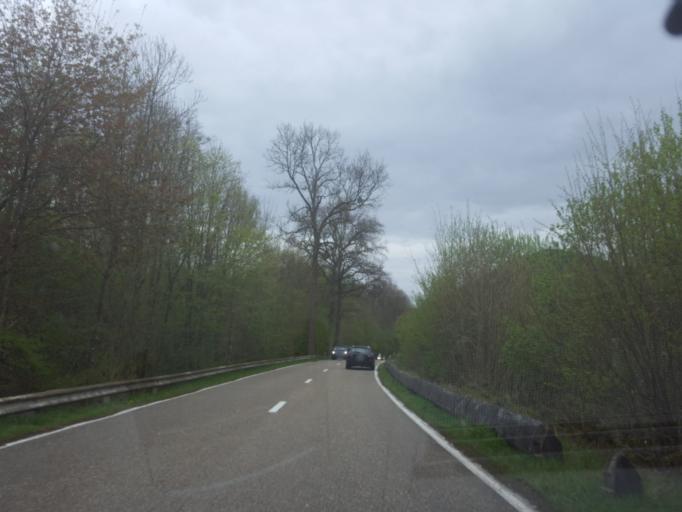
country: BE
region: Wallonia
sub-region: Province de Liege
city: Aywaille
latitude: 50.4434
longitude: 5.7381
